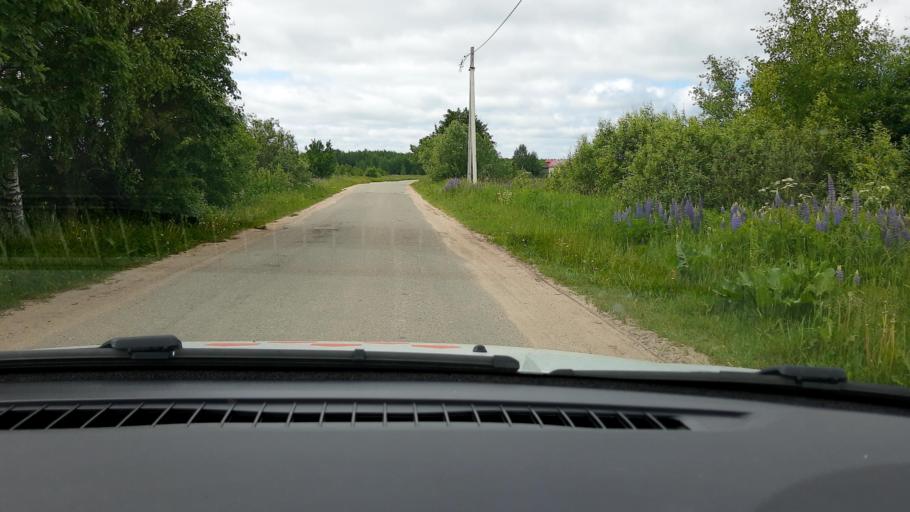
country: RU
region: Nizjnij Novgorod
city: Sitniki
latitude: 56.5178
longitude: 44.1105
